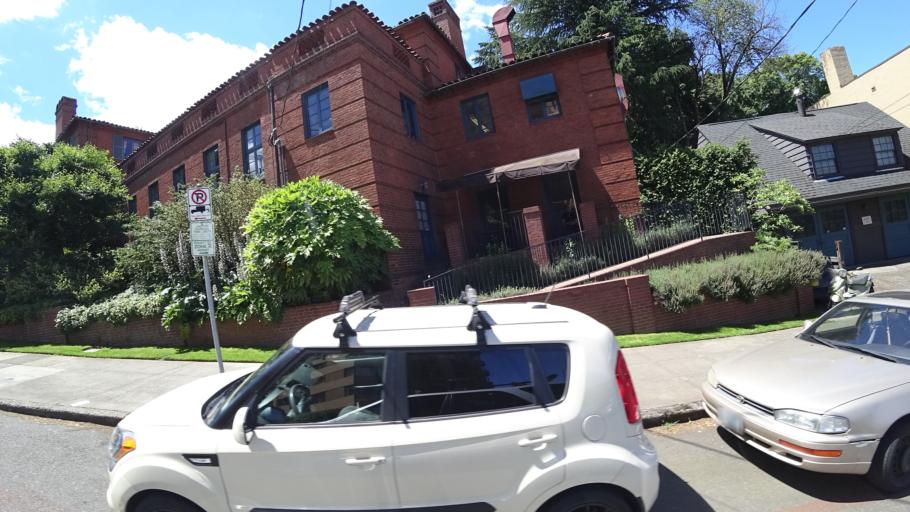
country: US
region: Oregon
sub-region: Multnomah County
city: Portland
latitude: 45.5212
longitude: -122.6942
